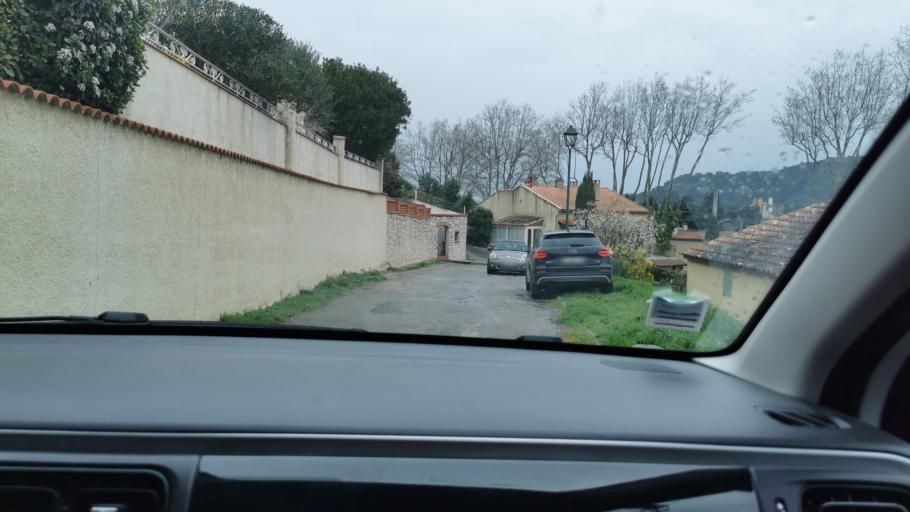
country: FR
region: Provence-Alpes-Cote d'Azur
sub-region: Departement des Bouches-du-Rhone
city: Lamanon
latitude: 43.7022
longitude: 5.0862
